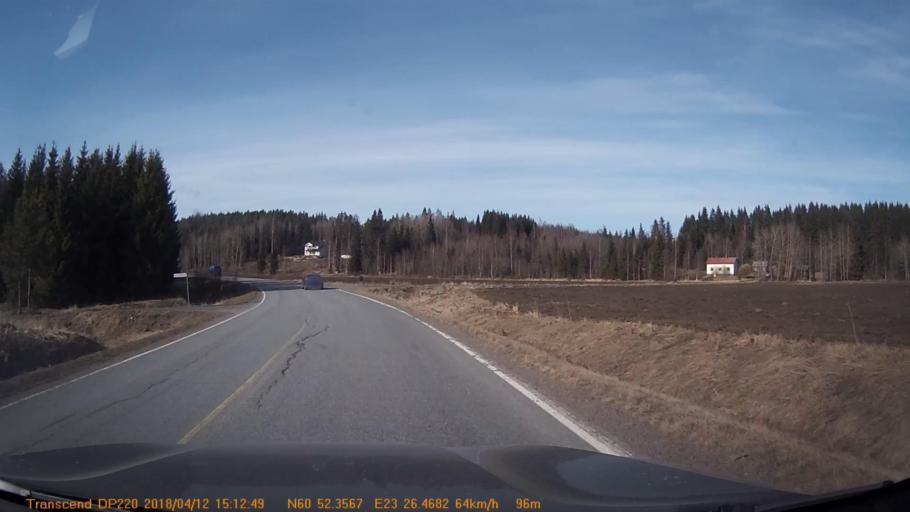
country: FI
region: Haeme
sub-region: Forssa
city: Jokioinen
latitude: 60.8725
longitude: 23.4413
